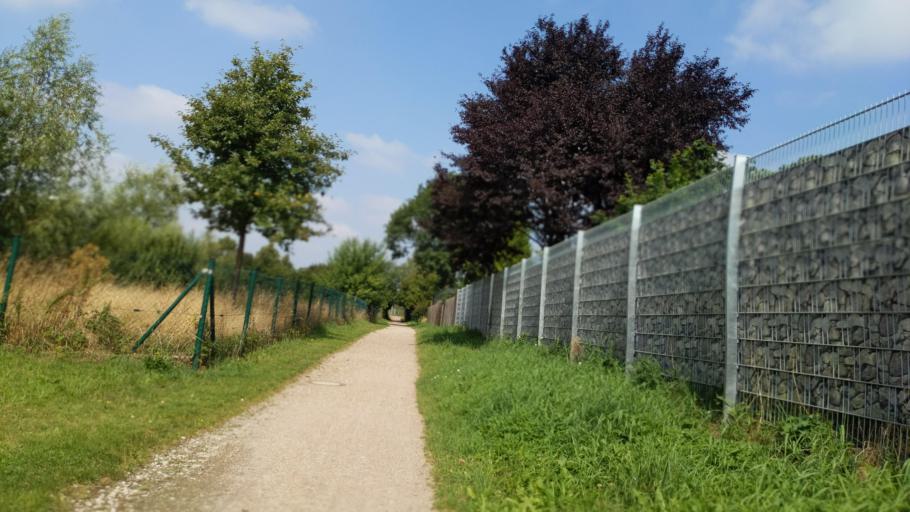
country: DE
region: Schleswig-Holstein
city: Stockelsdorf
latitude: 53.8897
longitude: 10.6312
